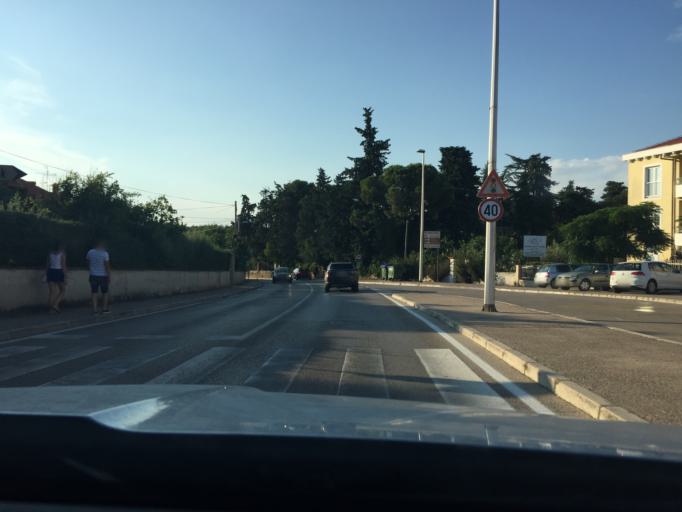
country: HR
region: Zadarska
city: Zadar
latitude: 44.1196
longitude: 15.2349
